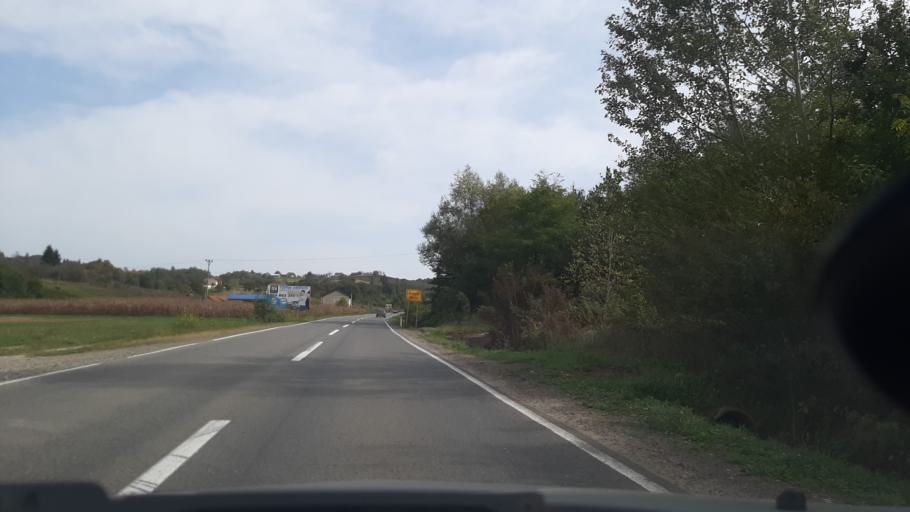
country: BA
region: Republika Srpska
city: Laktasi
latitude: 44.8748
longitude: 17.3174
